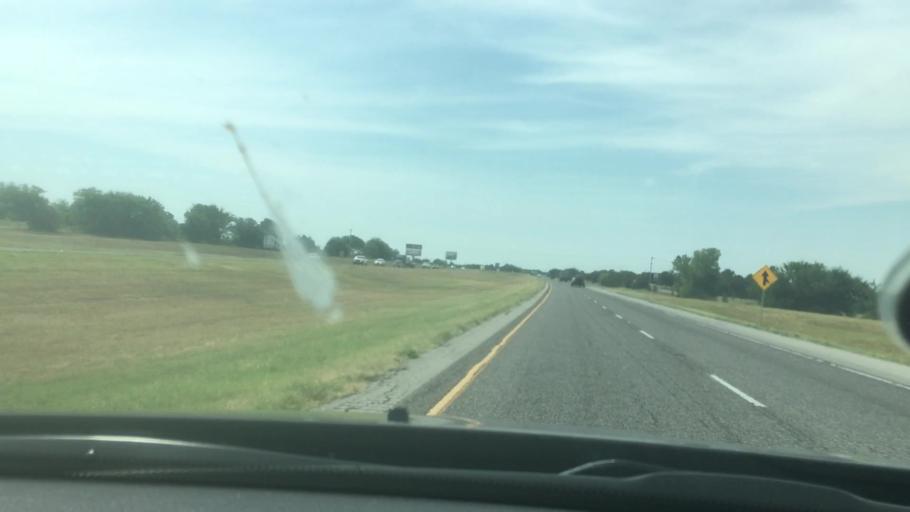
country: US
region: Oklahoma
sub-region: Garvin County
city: Wynnewood
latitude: 34.5700
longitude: -97.1985
